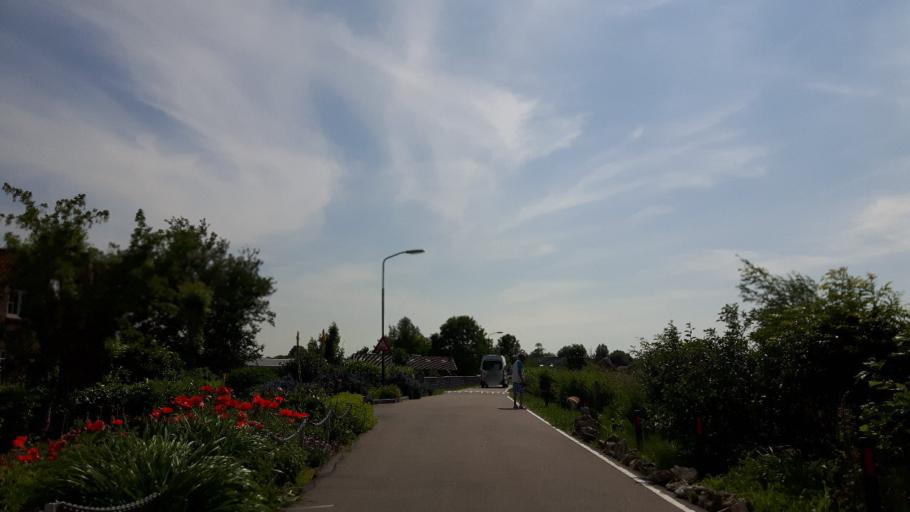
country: NL
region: North Holland
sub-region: Gemeente Uithoorn
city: Uithoorn
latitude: 52.2284
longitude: 4.8212
